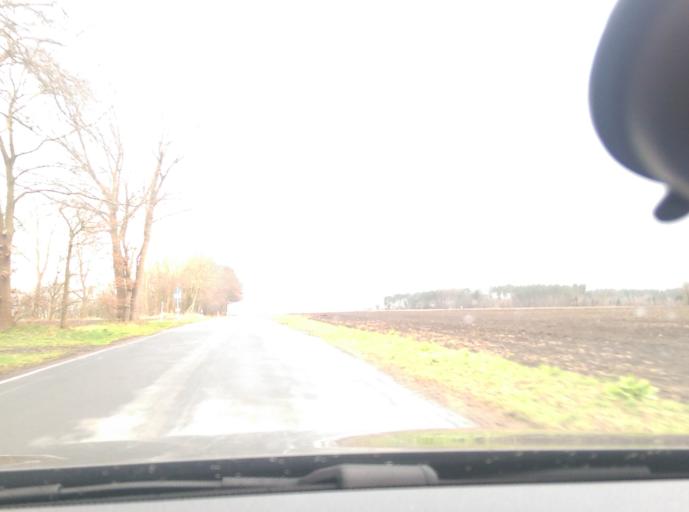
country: DE
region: Lower Saxony
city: Schwarmstedt
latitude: 52.6087
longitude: 9.6048
